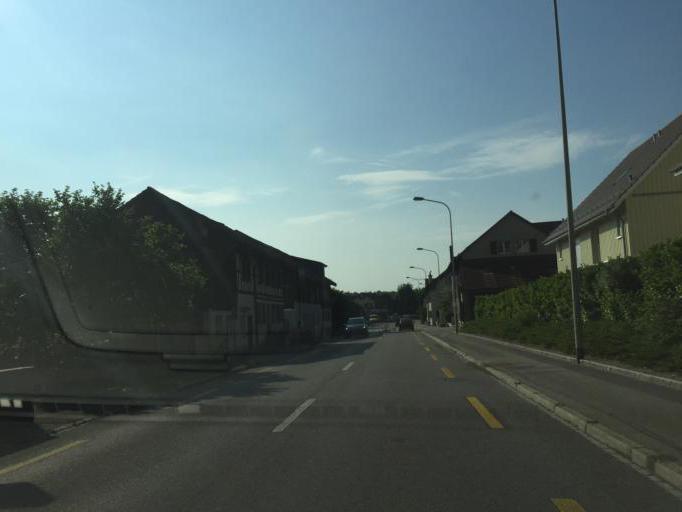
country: CH
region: Zurich
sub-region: Bezirk Buelach
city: Rorbas
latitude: 47.5329
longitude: 8.5722
